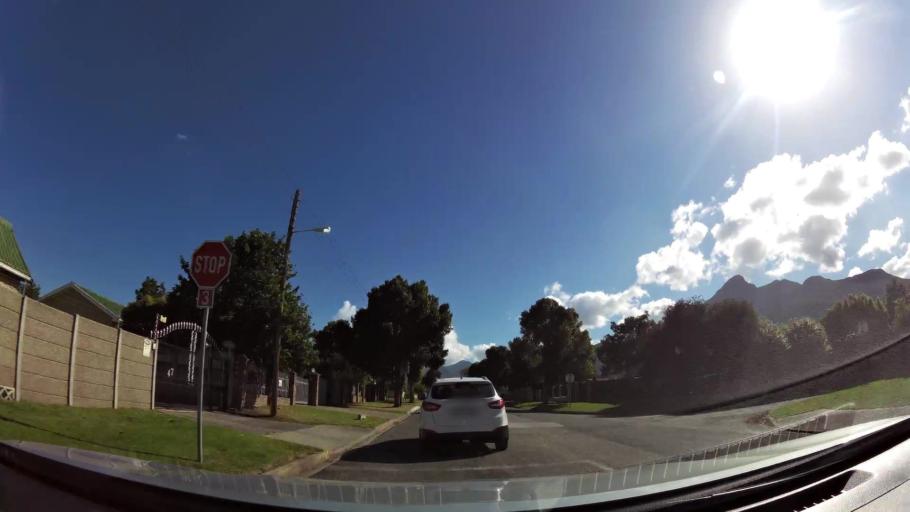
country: ZA
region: Western Cape
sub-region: Eden District Municipality
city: George
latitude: -33.9507
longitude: 22.4770
